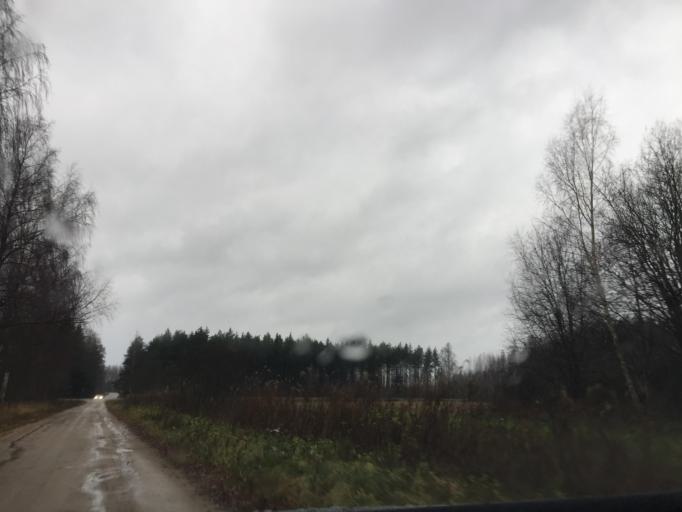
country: LV
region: Limbazu Rajons
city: Limbazi
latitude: 57.5499
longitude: 24.7610
